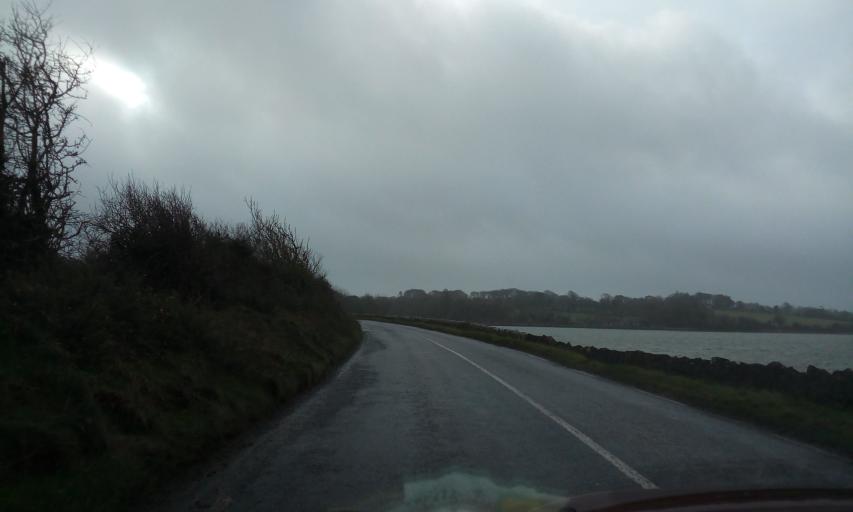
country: IE
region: Leinster
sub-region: Loch Garman
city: New Ross
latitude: 52.2509
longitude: -6.7543
